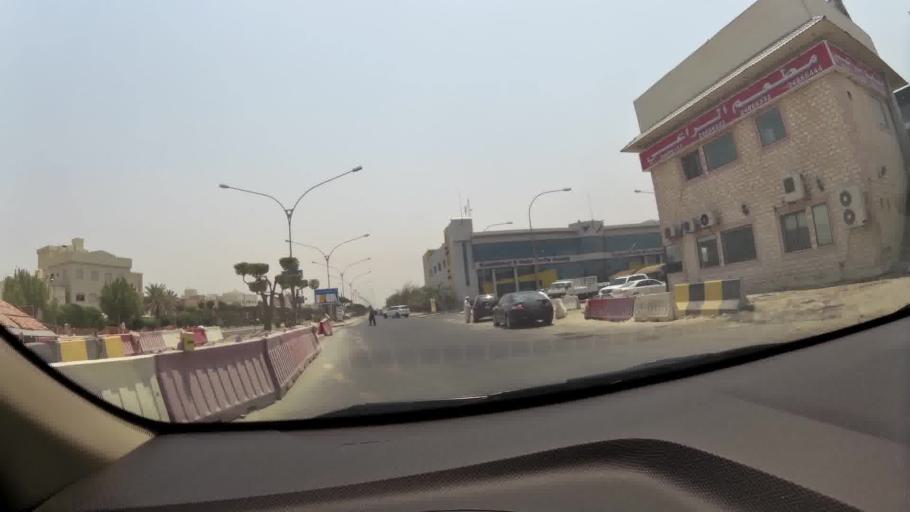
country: KW
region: Al Asimah
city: Ar Rabiyah
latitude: 29.3196
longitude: 47.8192
